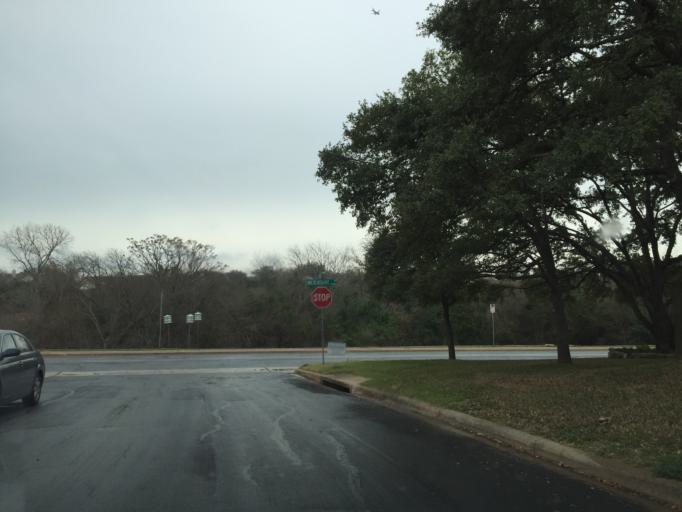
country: US
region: Texas
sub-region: Travis County
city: Wells Branch
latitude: 30.3992
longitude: -97.6928
